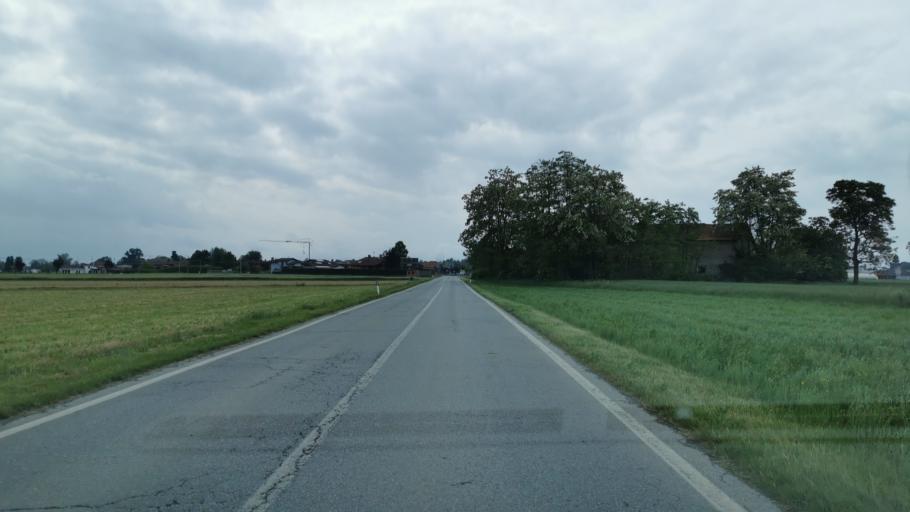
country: IT
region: Piedmont
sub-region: Provincia di Cuneo
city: Villafalletto
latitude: 44.5558
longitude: 7.5358
